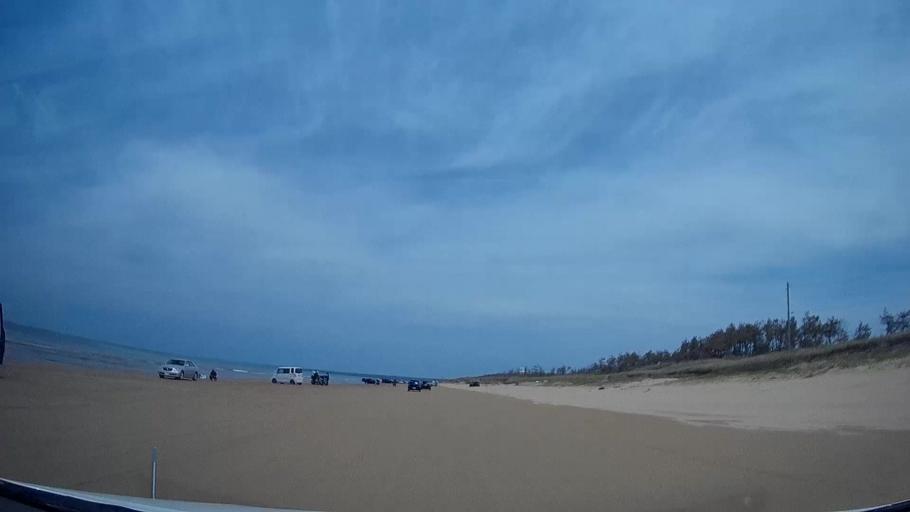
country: JP
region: Ishikawa
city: Hakui
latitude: 36.8432
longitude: 136.7506
